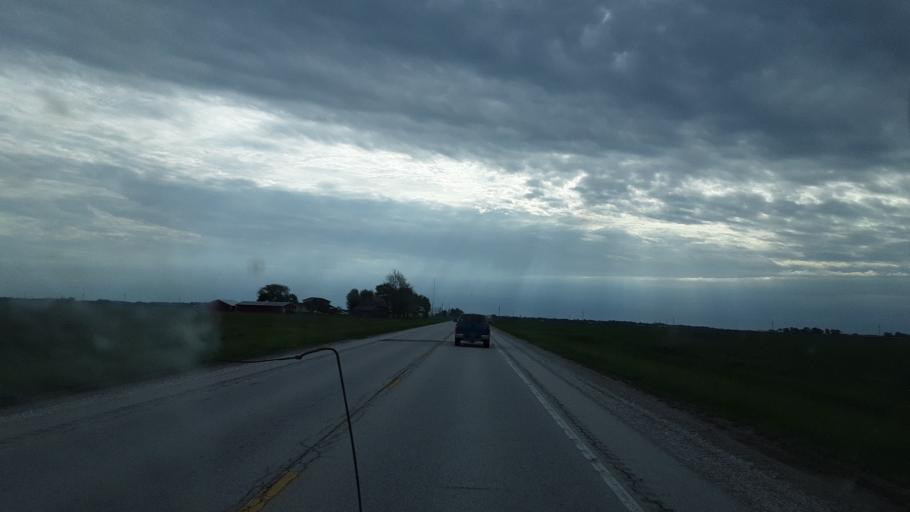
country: US
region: Illinois
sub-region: Hancock County
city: Carthage
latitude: 40.4041
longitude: -91.1873
